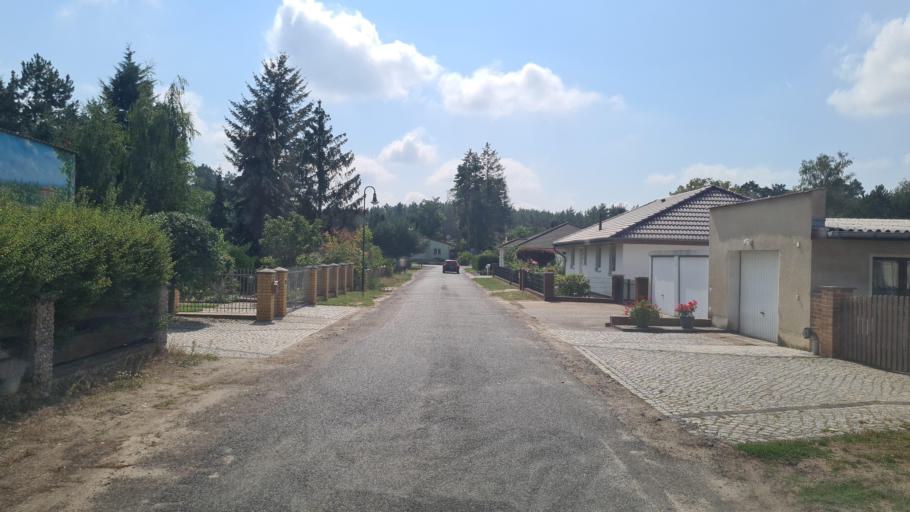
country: DE
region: Brandenburg
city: Am Mellensee
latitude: 52.2237
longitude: 13.3932
